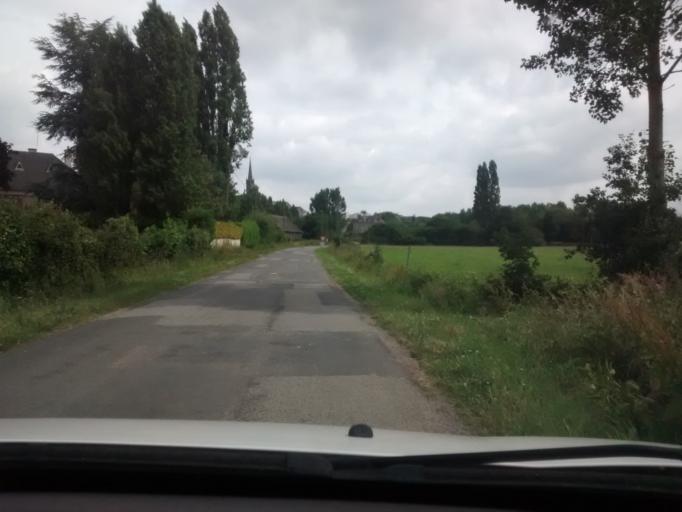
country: FR
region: Brittany
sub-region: Departement d'Ille-et-Vilaine
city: Acigne
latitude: 48.1283
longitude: -1.5356
